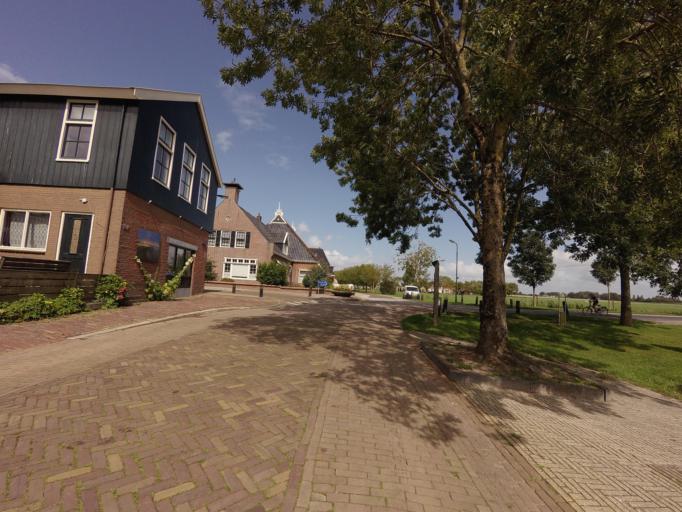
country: NL
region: Friesland
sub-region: Gemeente Harlingen
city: Harlingen
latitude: 53.1150
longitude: 5.4414
